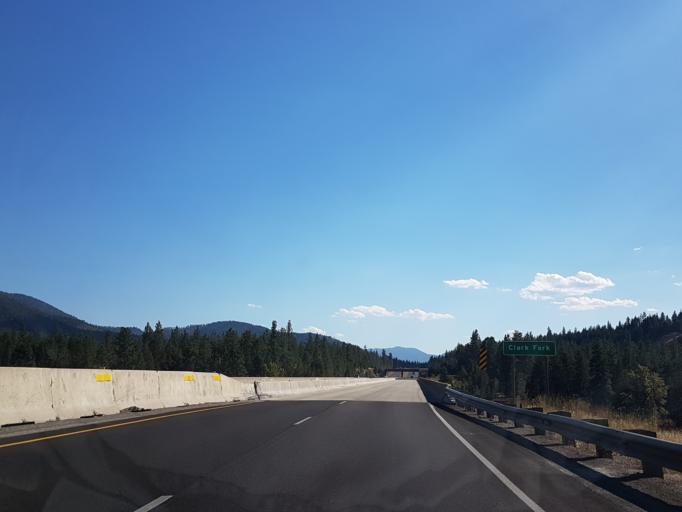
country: US
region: Montana
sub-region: Mineral County
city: Superior
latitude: 47.1324
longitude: -114.7975
